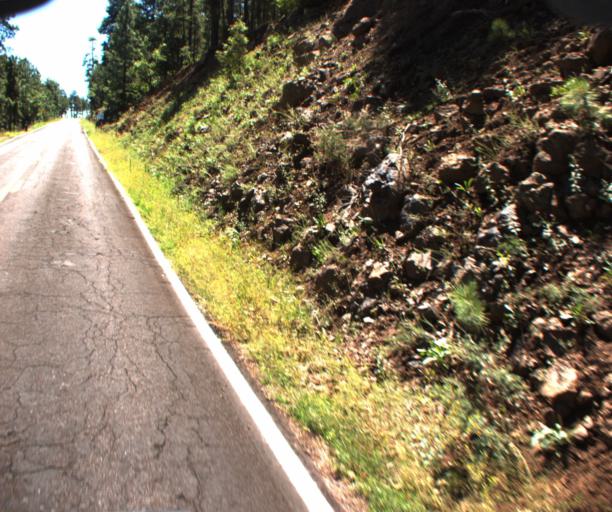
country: US
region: Arizona
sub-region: Greenlee County
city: Morenci
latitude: 33.4674
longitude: -109.3628
